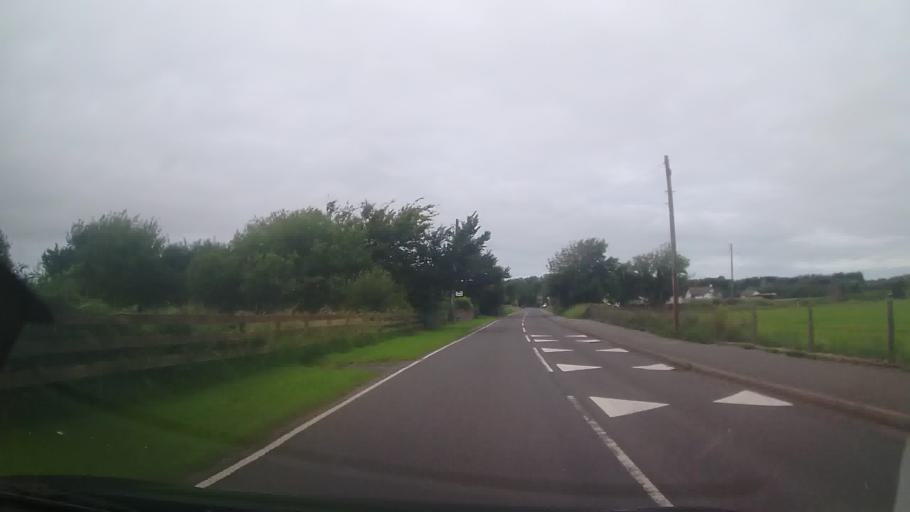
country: GB
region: Wales
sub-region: Gwynedd
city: Caernarfon
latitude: 53.1643
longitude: -4.3310
